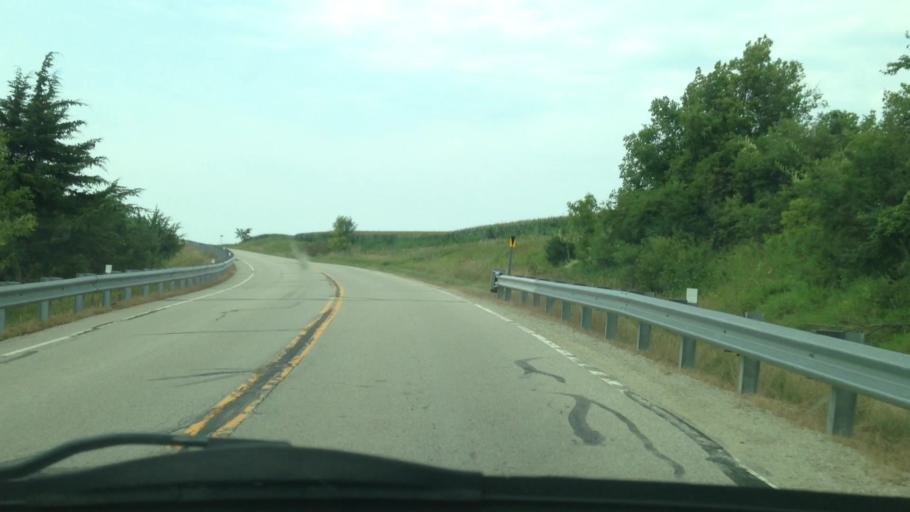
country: US
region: Minnesota
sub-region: Fillmore County
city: Preston
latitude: 43.7543
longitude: -91.9639
